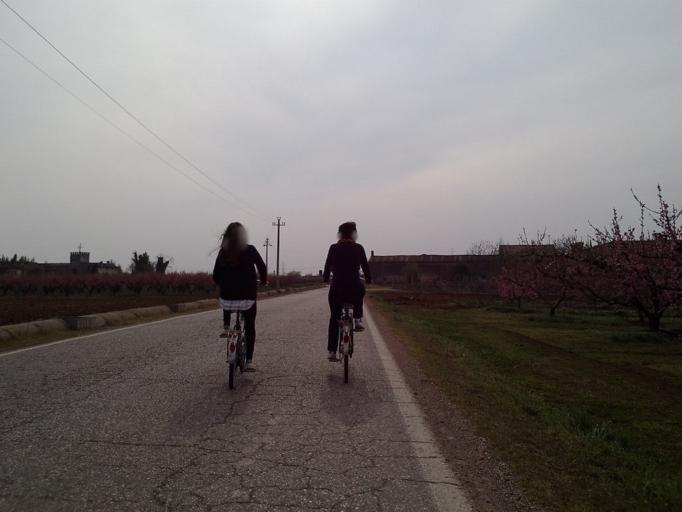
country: IT
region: Veneto
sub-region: Provincia di Verona
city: Alpo
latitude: 45.3767
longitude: 10.9013
